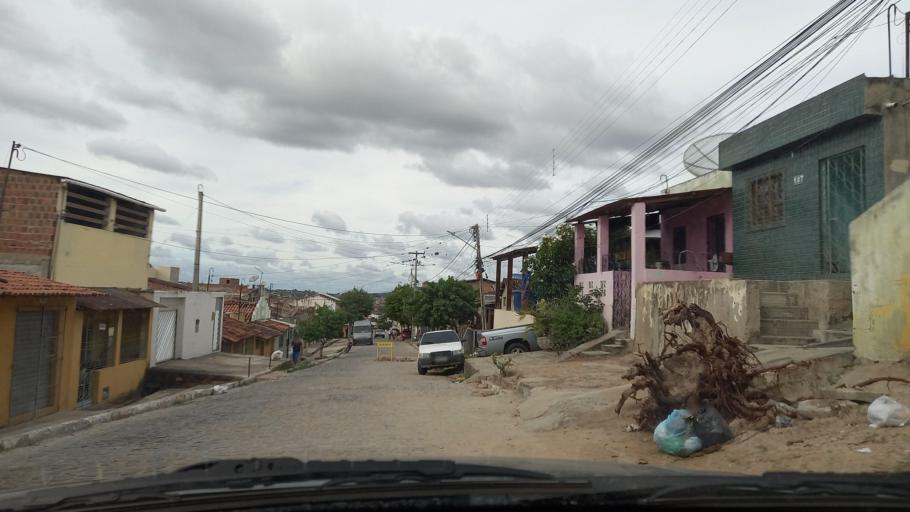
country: BR
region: Pernambuco
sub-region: Gravata
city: Gravata
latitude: -8.2087
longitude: -35.5727
